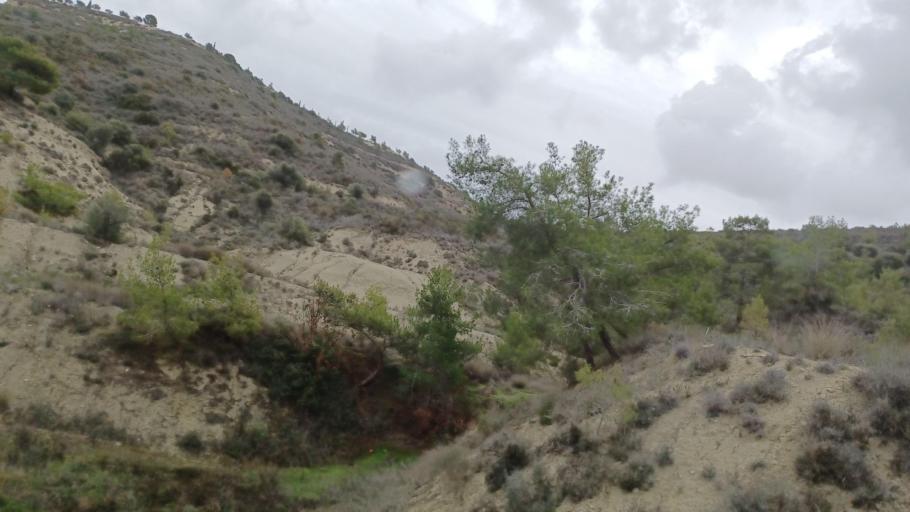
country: CY
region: Limassol
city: Pyrgos
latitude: 34.7722
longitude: 33.2563
